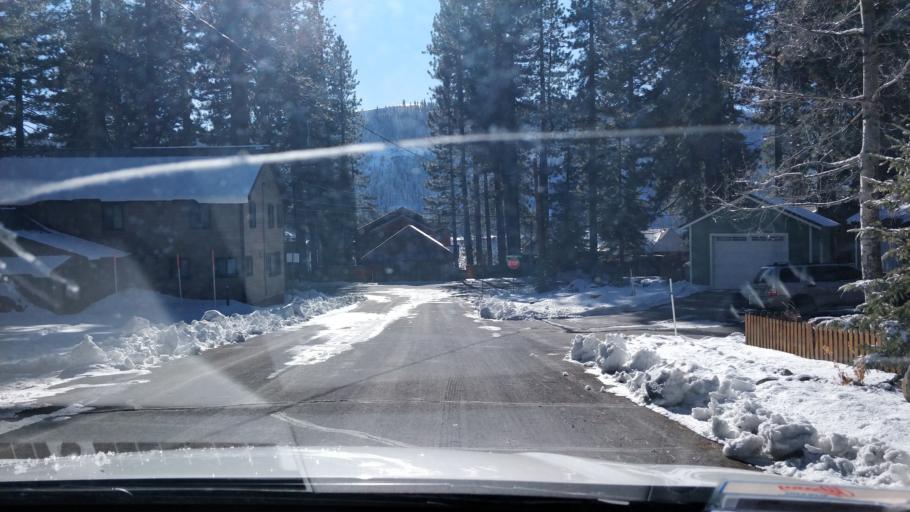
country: US
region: California
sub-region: Nevada County
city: Truckee
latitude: 39.3293
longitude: -120.2483
